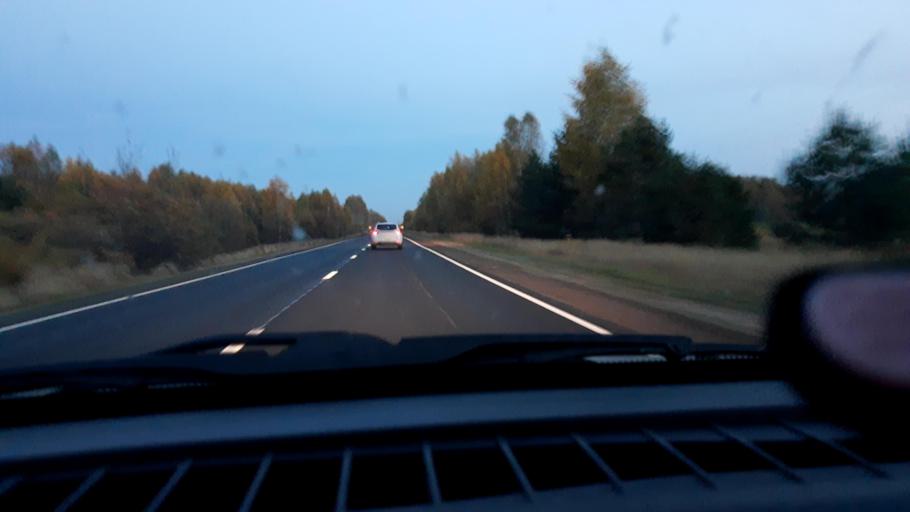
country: RU
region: Nizjnij Novgorod
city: Novaya Balakhna
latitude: 56.5929
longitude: 43.6552
